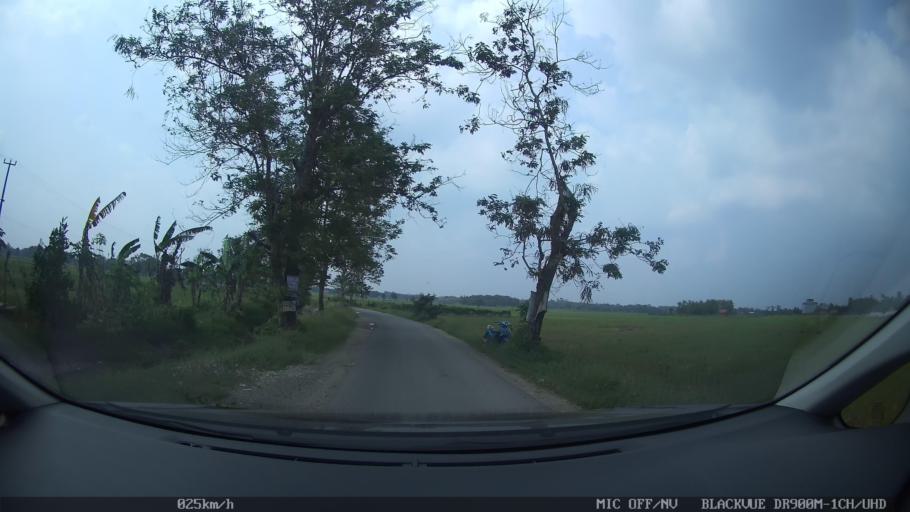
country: ID
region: Lampung
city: Gadingrejo
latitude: -5.3694
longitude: 105.0512
